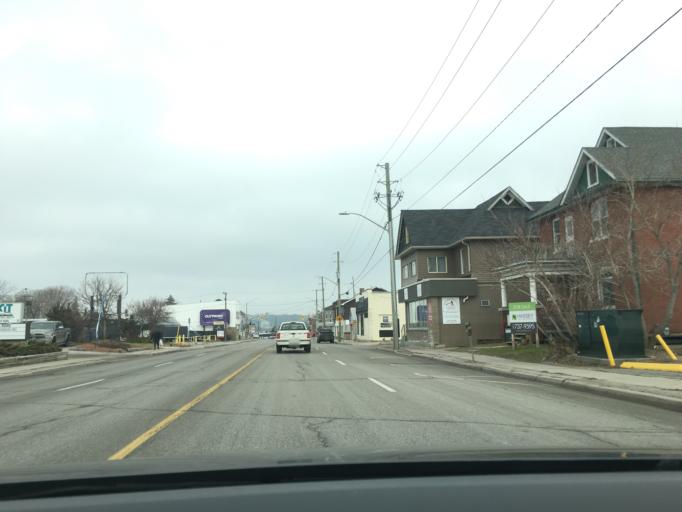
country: CA
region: Ontario
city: Barrie
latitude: 44.3724
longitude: -79.6919
